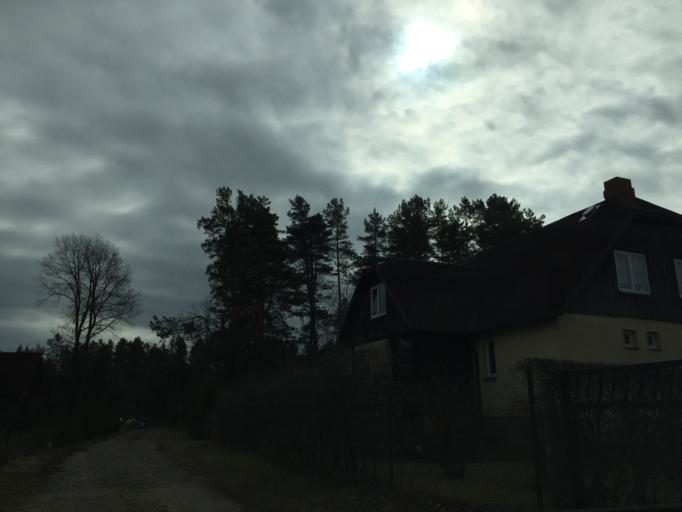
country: LV
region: Garkalne
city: Garkalne
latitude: 57.0737
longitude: 24.4258
